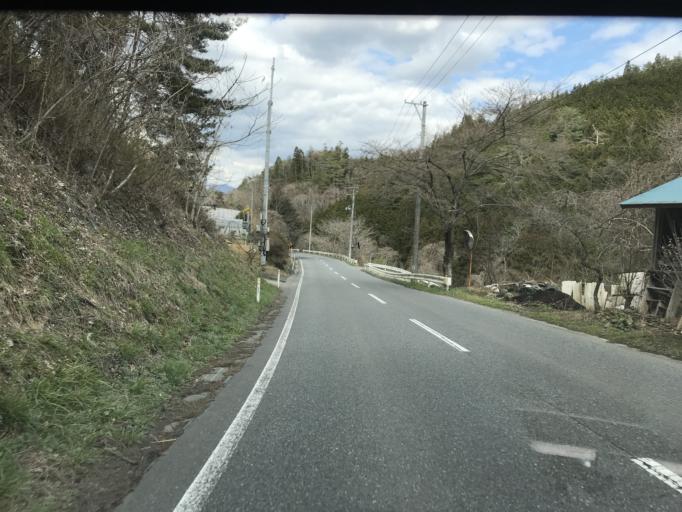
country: JP
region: Iwate
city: Ichinoseki
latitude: 38.8223
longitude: 141.3280
